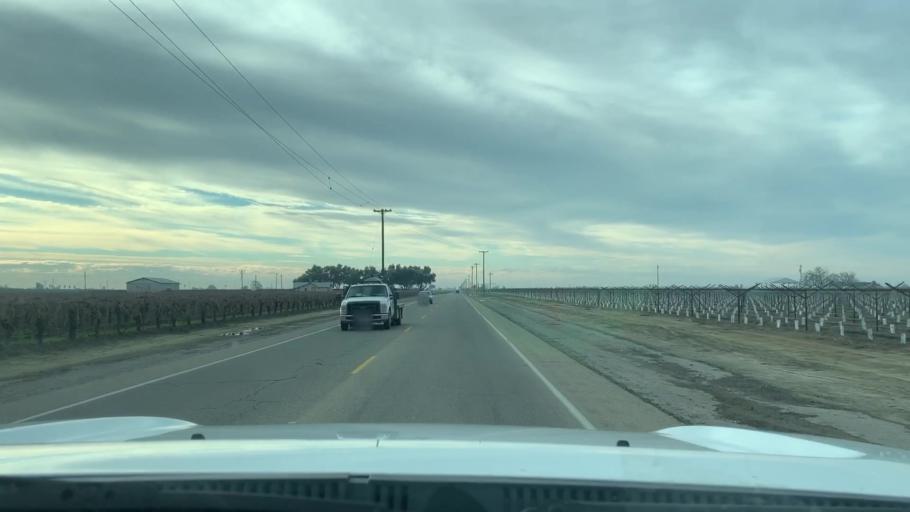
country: US
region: California
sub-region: Fresno County
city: Fowler
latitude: 36.6055
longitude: -119.6961
